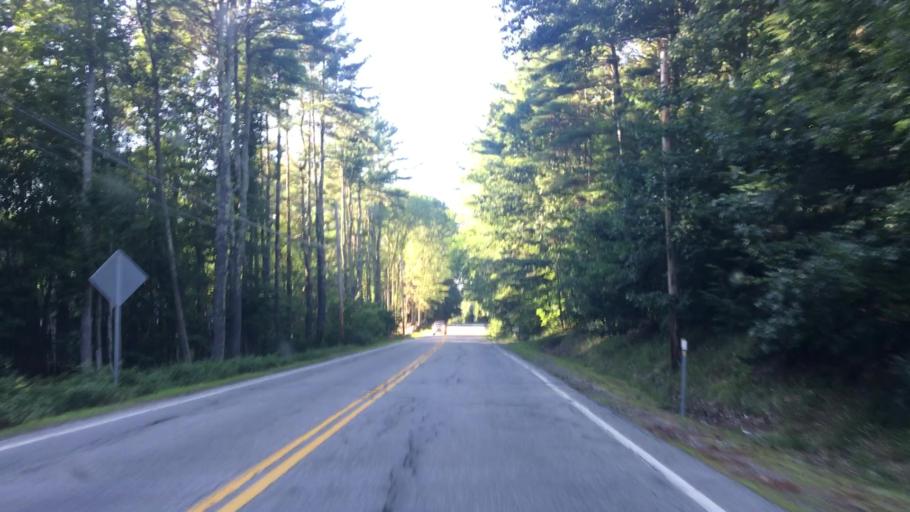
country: US
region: New Hampshire
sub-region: Rockingham County
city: Sandown
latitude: 42.9396
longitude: -71.1932
